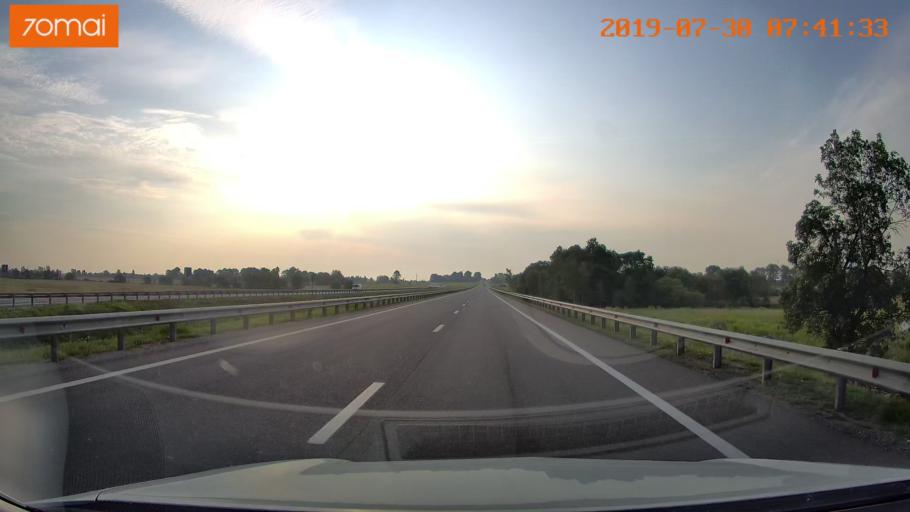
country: RU
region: Kaliningrad
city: Gvardeysk
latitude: 54.6482
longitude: 21.2542
